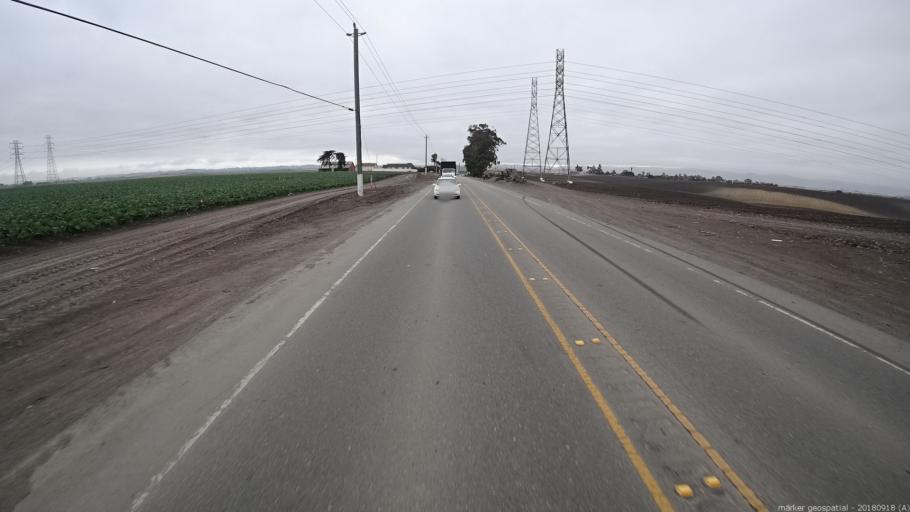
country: US
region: California
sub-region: Monterey County
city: Castroville
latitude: 36.7461
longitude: -121.7264
